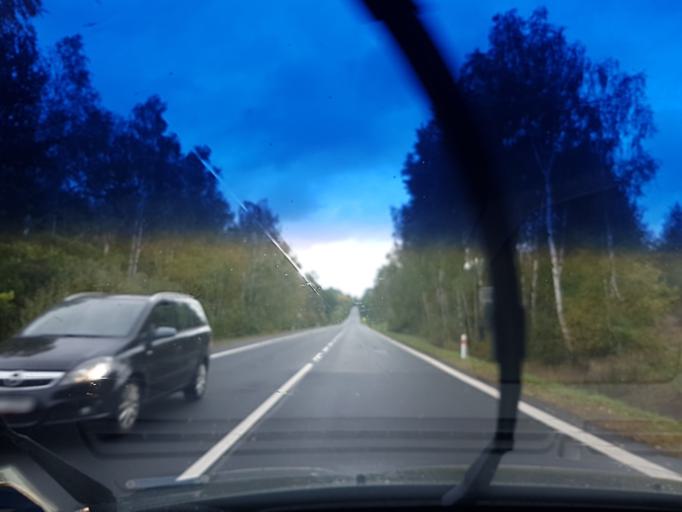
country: DE
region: Bavaria
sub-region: Upper Franconia
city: Schirnding
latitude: 50.0859
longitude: 12.2901
